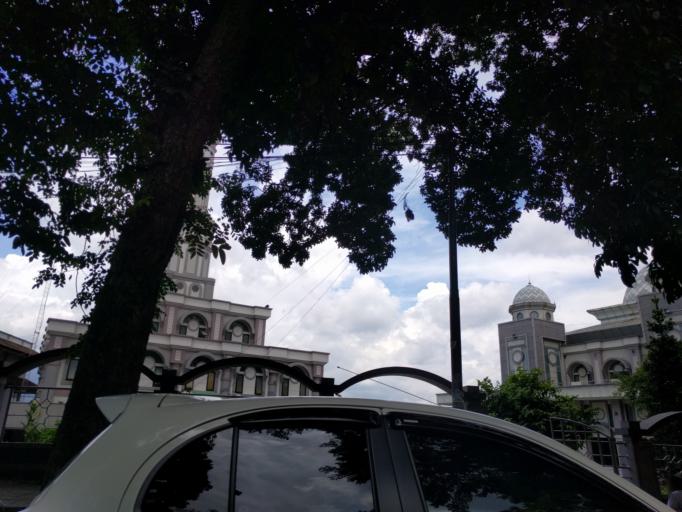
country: ID
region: West Java
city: Bogor
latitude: -6.6073
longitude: 106.8092
